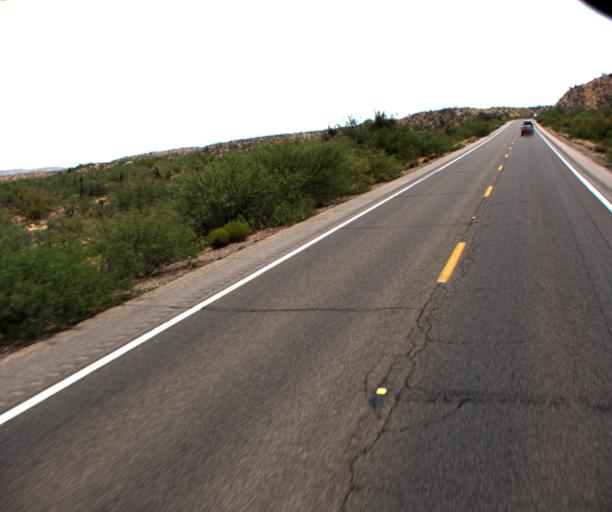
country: US
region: Arizona
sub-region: Gila County
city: San Carlos
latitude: 33.3442
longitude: -110.6134
